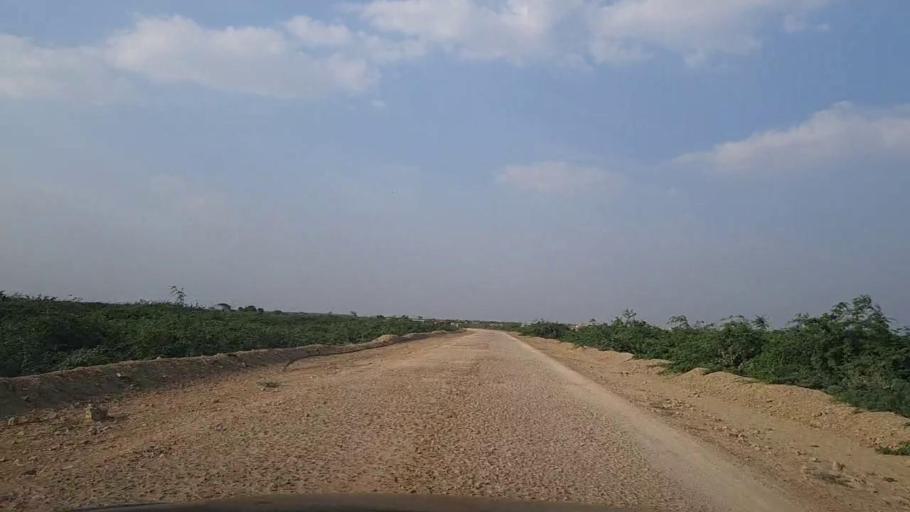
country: PK
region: Sindh
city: Gharo
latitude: 24.7966
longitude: 67.7447
